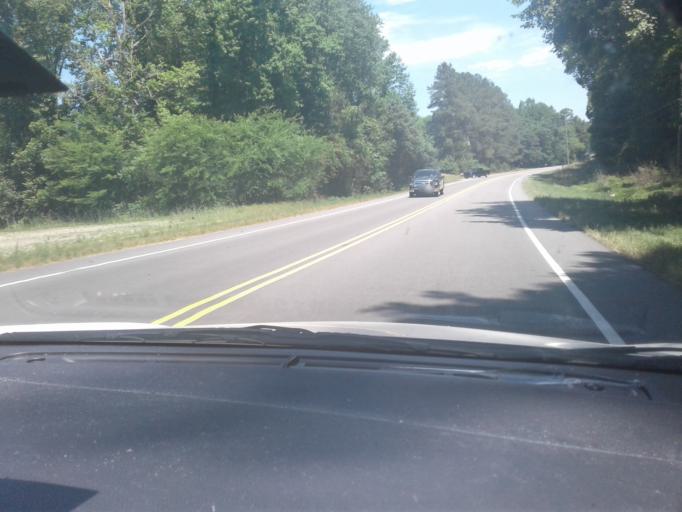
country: US
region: North Carolina
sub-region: Harnett County
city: Lillington
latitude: 35.4593
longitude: -78.8303
